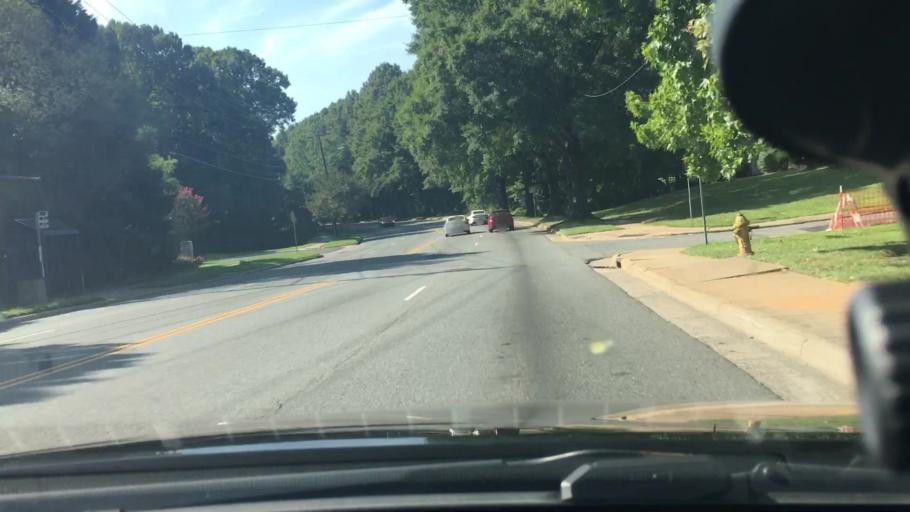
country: US
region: North Carolina
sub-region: Mecklenburg County
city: Matthews
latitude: 35.1974
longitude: -80.7265
